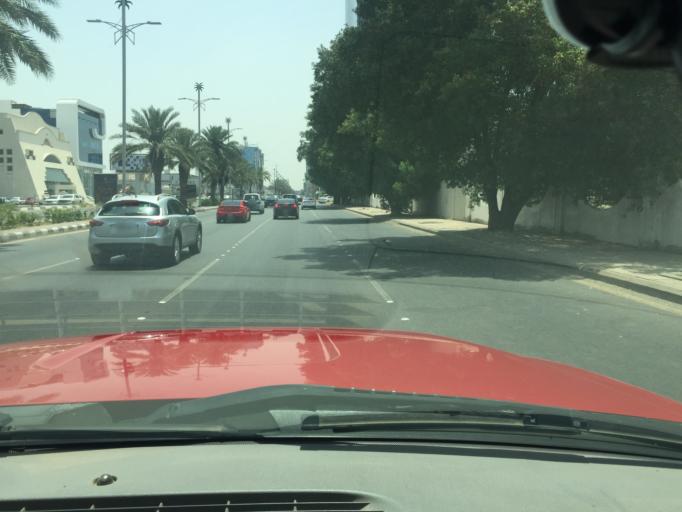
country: SA
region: Makkah
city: Jeddah
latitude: 21.5518
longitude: 39.1601
